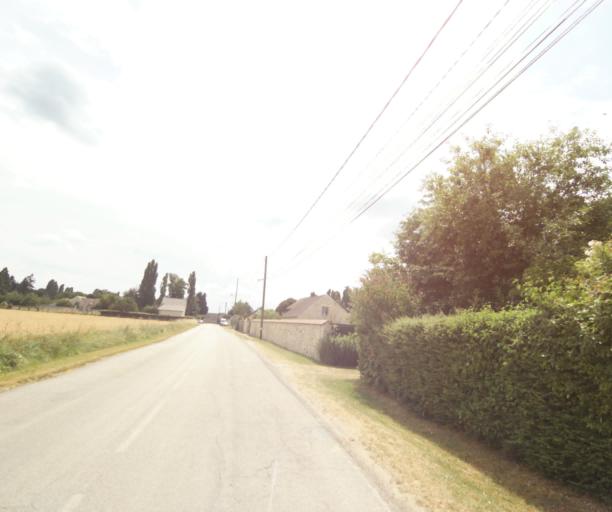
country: FR
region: Ile-de-France
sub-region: Departement de Seine-et-Marne
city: Barbizon
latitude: 48.4337
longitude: 2.5880
